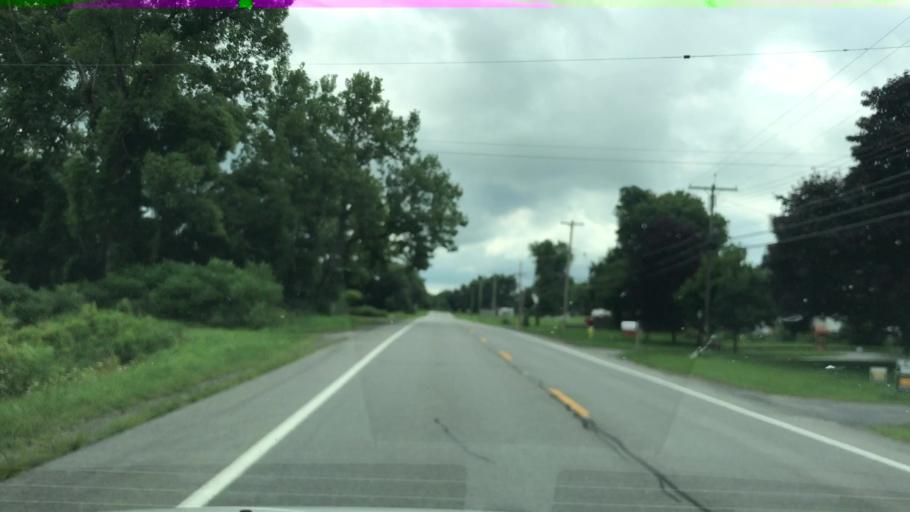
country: US
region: New York
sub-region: Livingston County
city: Mount Morris
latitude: 42.7094
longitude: -77.8637
